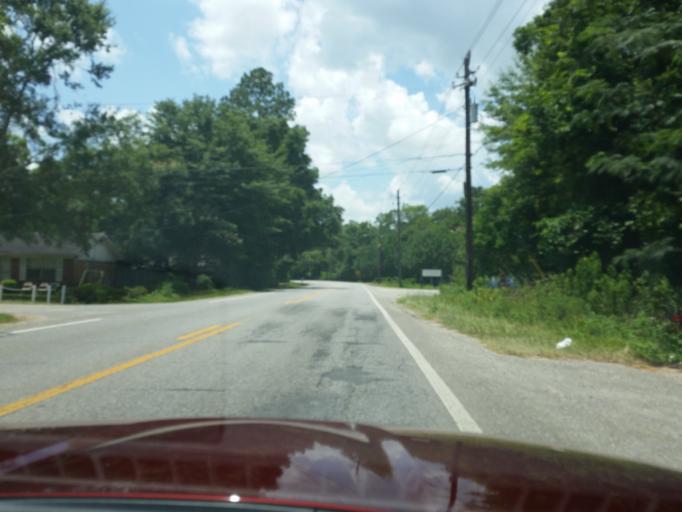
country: US
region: Florida
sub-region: Escambia County
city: Gonzalez
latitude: 30.5822
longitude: -87.2882
